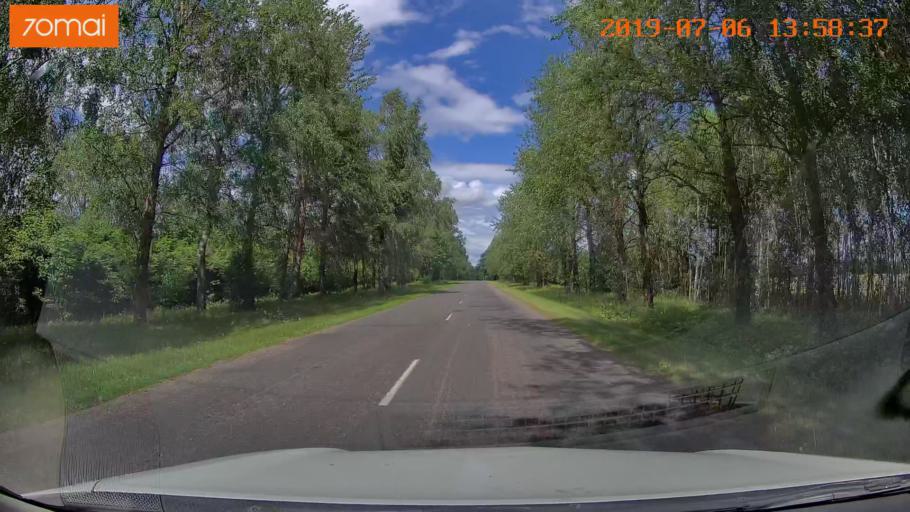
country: BY
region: Minsk
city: Ivyanyets
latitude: 53.7861
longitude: 26.8096
